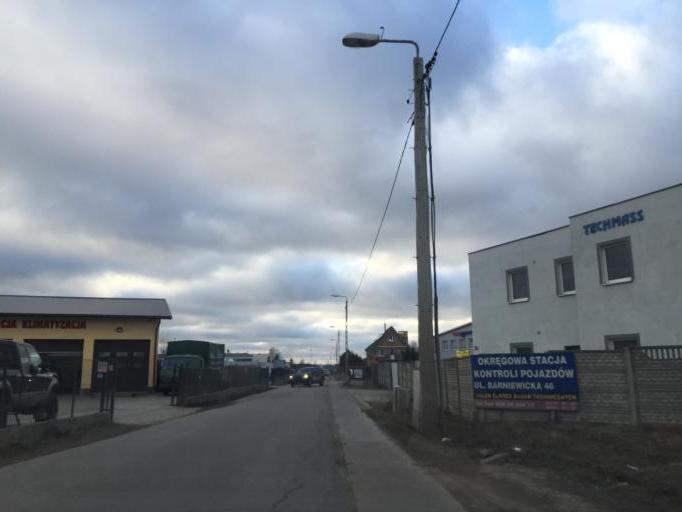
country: PL
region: Pomeranian Voivodeship
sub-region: Powiat kartuski
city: Chwaszczyno
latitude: 54.4160
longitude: 18.4632
